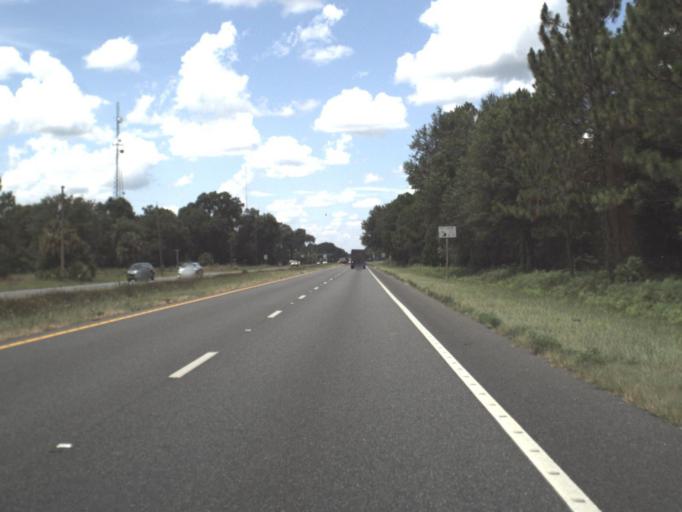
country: US
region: Florida
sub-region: Taylor County
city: Perry
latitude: 30.1416
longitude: -83.6077
